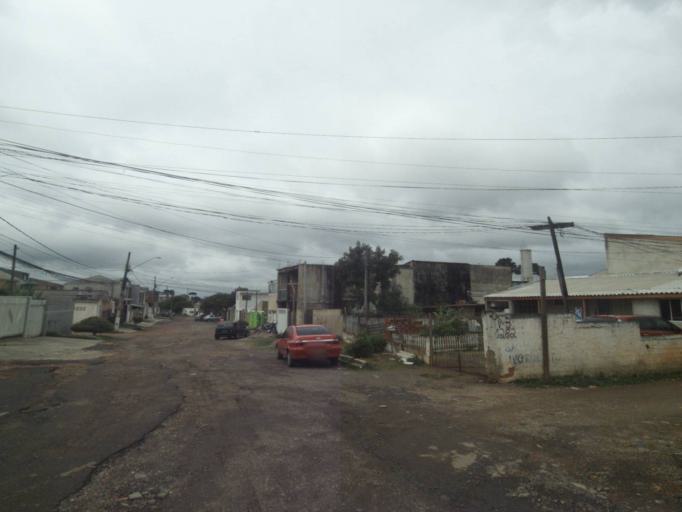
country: BR
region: Parana
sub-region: Curitiba
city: Curitiba
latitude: -25.4972
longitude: -49.3010
